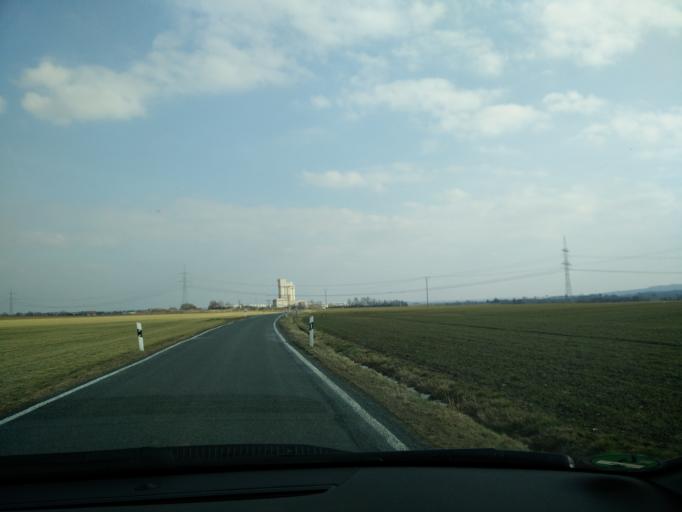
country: DE
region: Saxony
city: Konigsfeld
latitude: 51.1034
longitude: 12.7376
